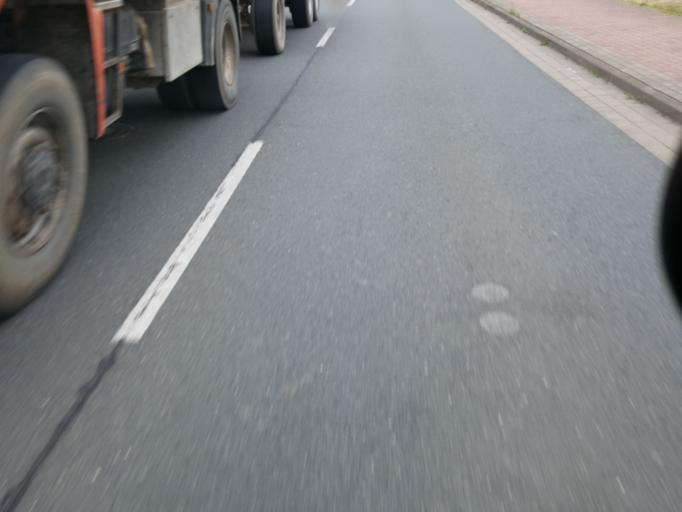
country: DE
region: Lower Saxony
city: Leese
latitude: 52.4601
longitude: 9.1477
